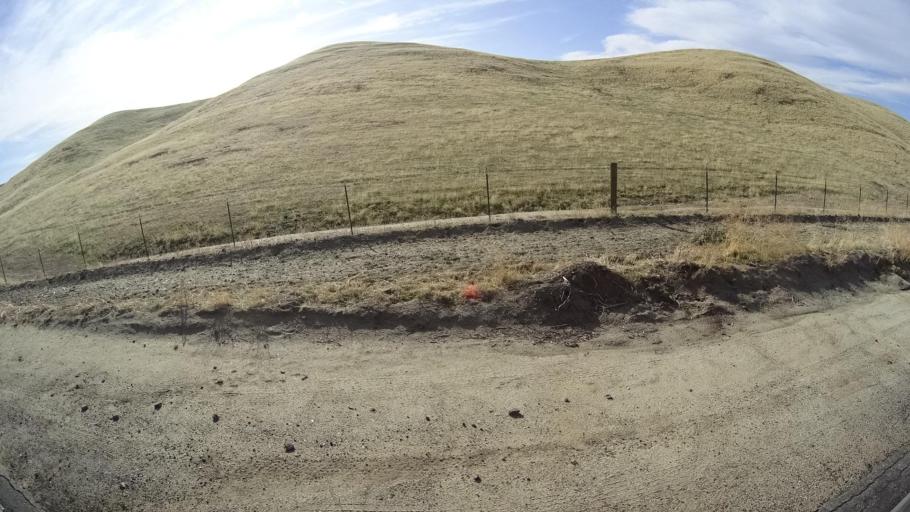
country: US
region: California
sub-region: Kern County
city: Oildale
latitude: 35.6115
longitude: -118.9357
